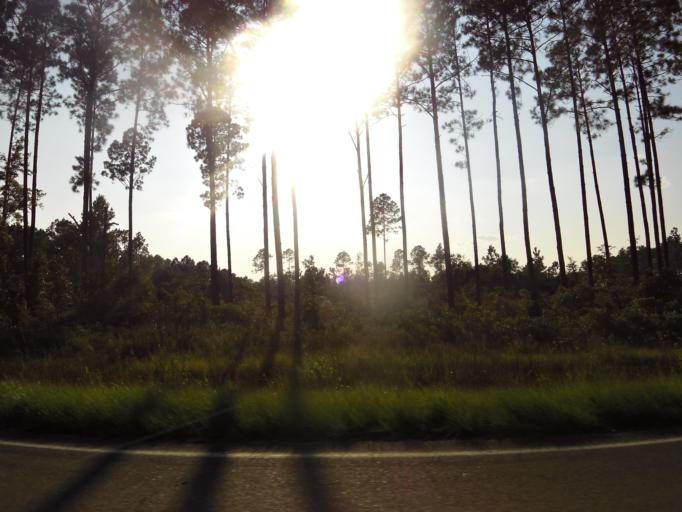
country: US
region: Florida
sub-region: Duval County
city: Baldwin
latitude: 30.3105
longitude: -82.0084
